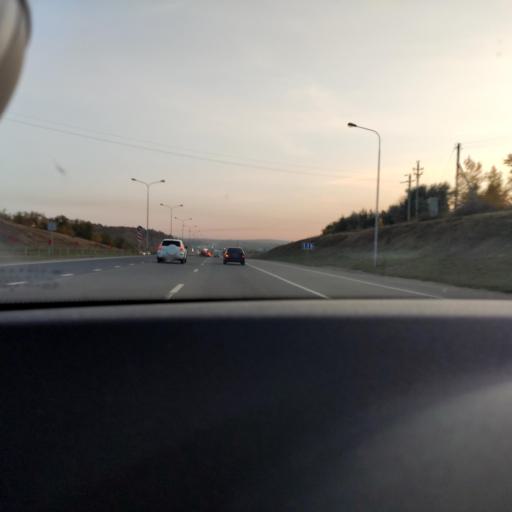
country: RU
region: Samara
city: Novosemeykino
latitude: 53.4060
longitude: 50.3347
